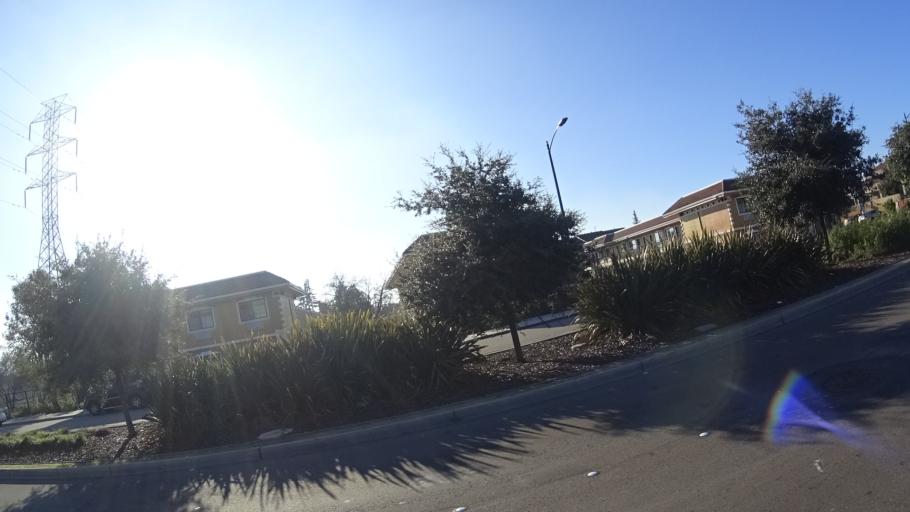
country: US
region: California
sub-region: Alameda County
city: Hayward
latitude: 37.6590
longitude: -122.0729
